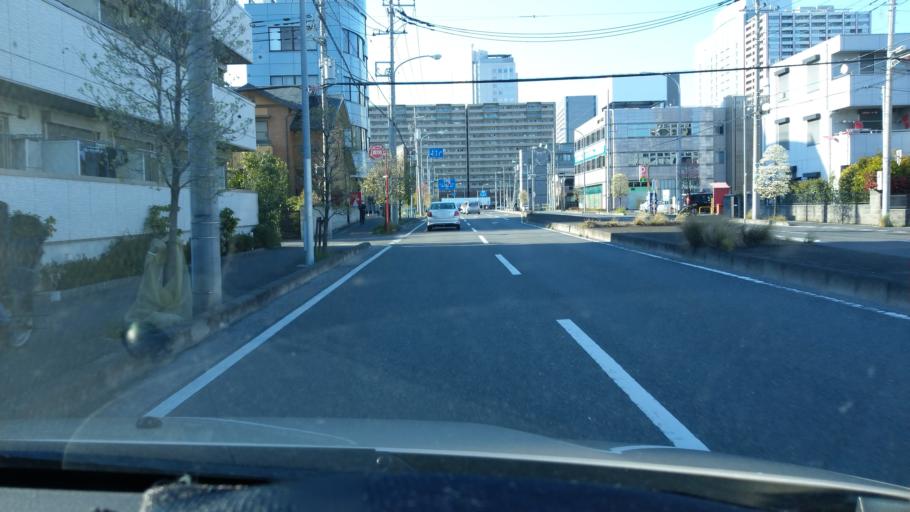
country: JP
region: Saitama
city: Yono
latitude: 35.9000
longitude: 139.6196
